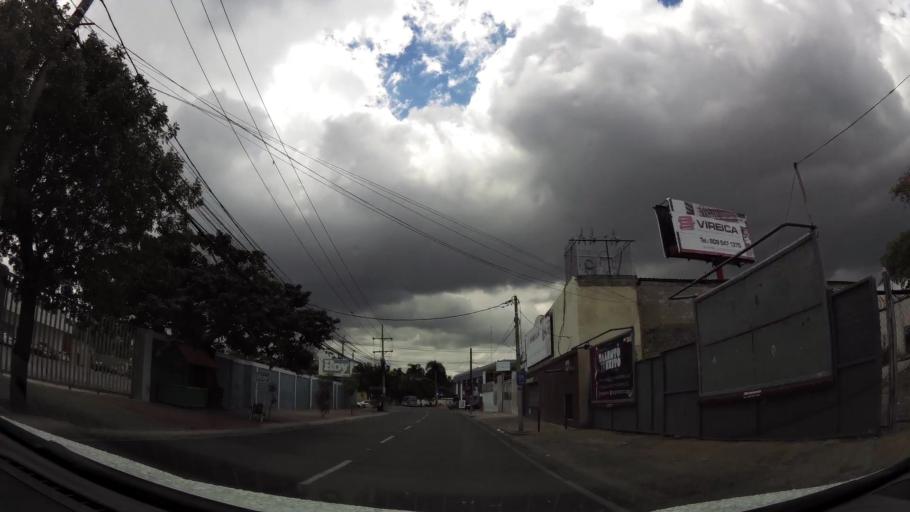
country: DO
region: Nacional
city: La Agustina
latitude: 18.4852
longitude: -69.9202
